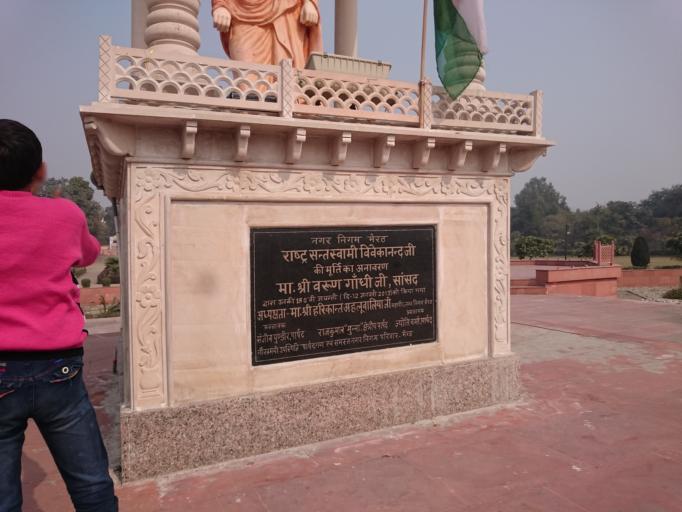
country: IN
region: Uttar Pradesh
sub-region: Meerut
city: Meerut
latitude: 28.9757
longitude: 77.7198
